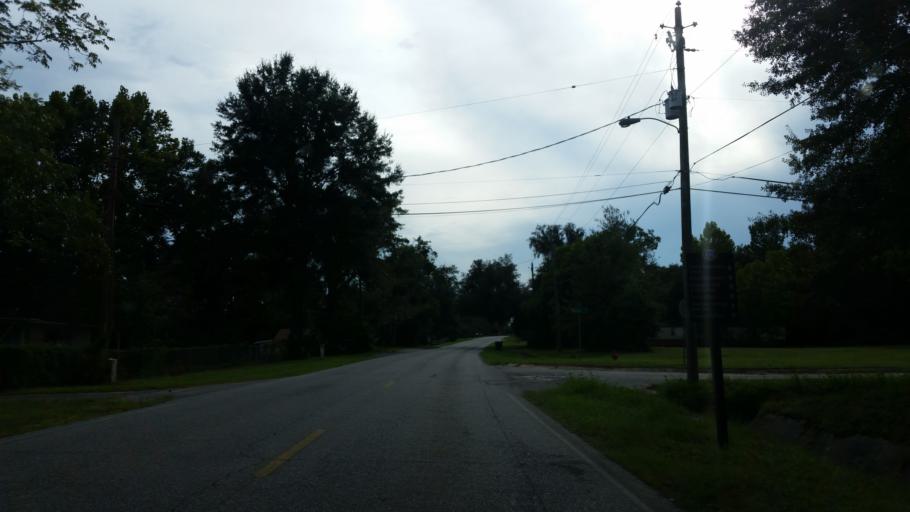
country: US
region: Florida
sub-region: Santa Rosa County
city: Milton
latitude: 30.6361
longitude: -87.0307
